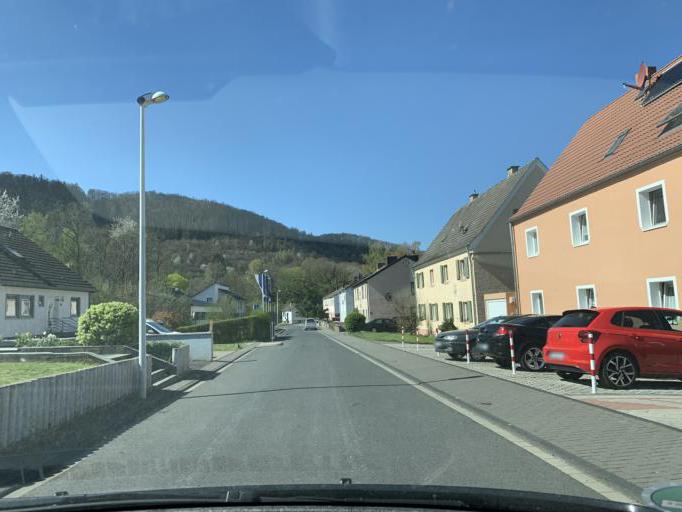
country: DE
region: North Rhine-Westphalia
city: Heimbach
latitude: 50.6326
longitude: 6.4577
